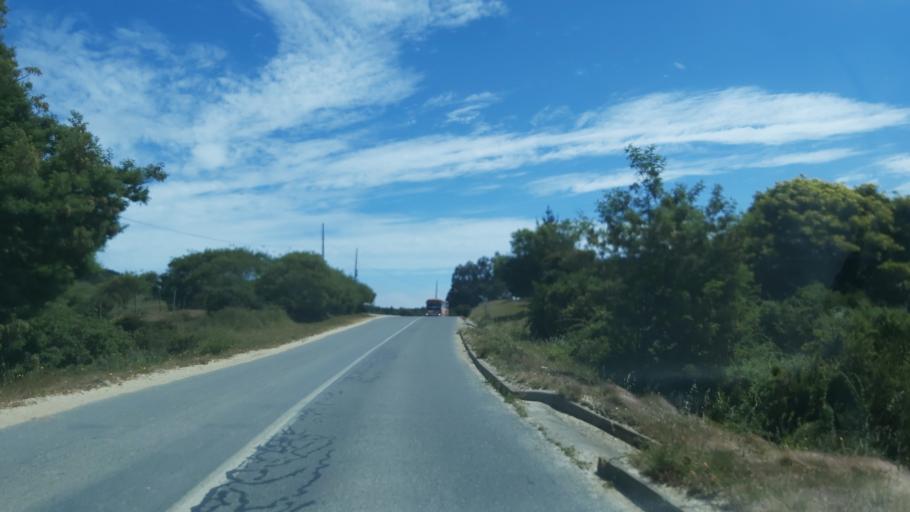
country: CL
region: Maule
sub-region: Provincia de Talca
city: Constitucion
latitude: -35.5643
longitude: -72.5936
